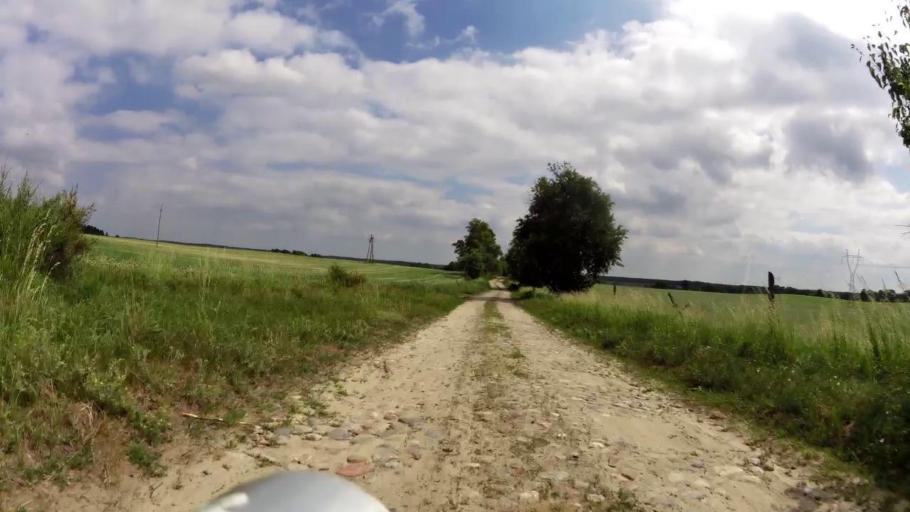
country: PL
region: West Pomeranian Voivodeship
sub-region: Powiat szczecinecki
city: Bialy Bor
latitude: 53.9562
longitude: 16.7727
